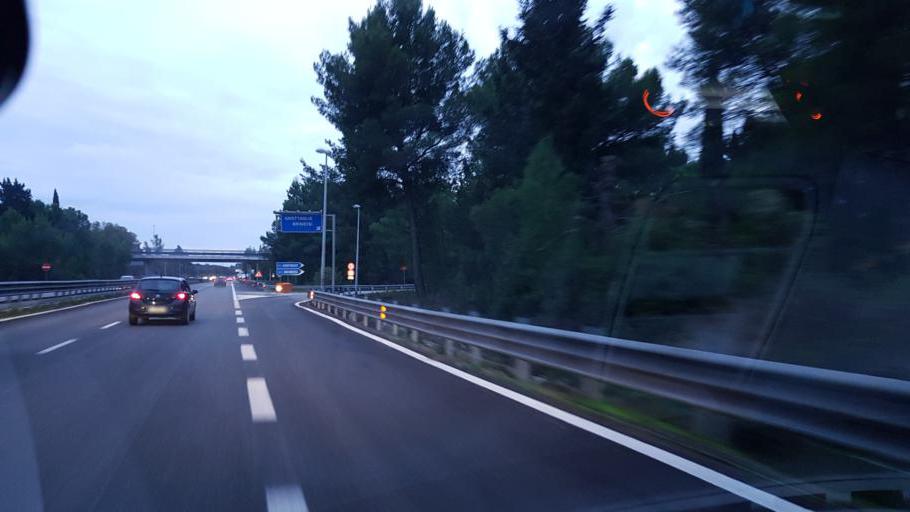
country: IT
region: Apulia
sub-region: Provincia di Taranto
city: Paolo VI
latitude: 40.5052
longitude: 17.2647
